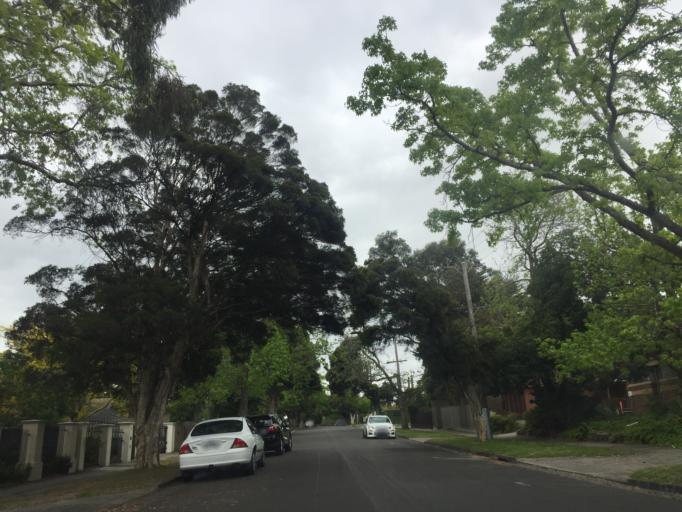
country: AU
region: Victoria
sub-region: Boroondara
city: Kew East
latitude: -37.8115
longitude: 145.0520
